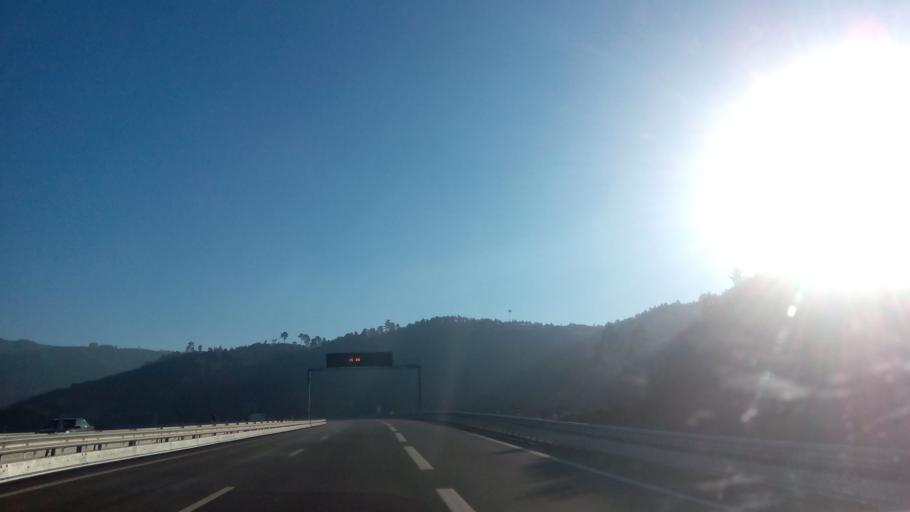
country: PT
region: Porto
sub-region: Amarante
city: Amarante
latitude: 41.2548
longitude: -7.9956
